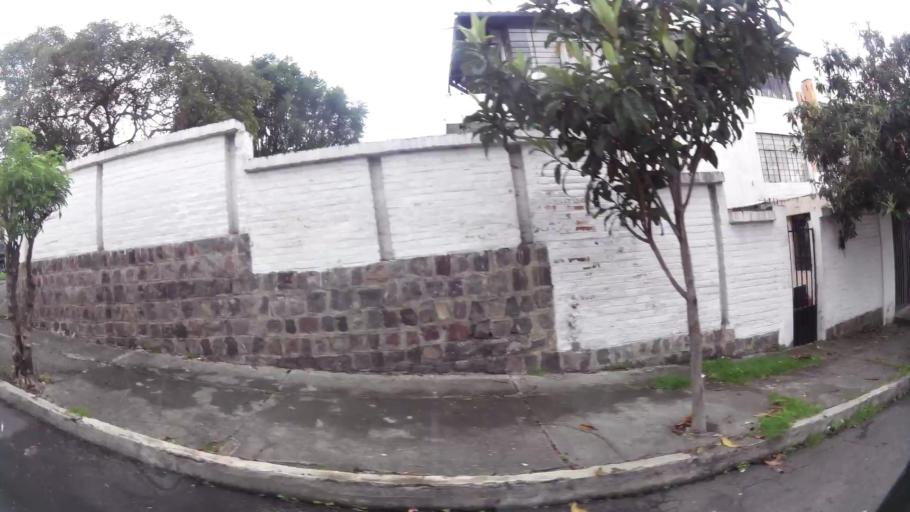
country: EC
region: Pichincha
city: Quito
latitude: -0.1880
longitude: -78.5014
